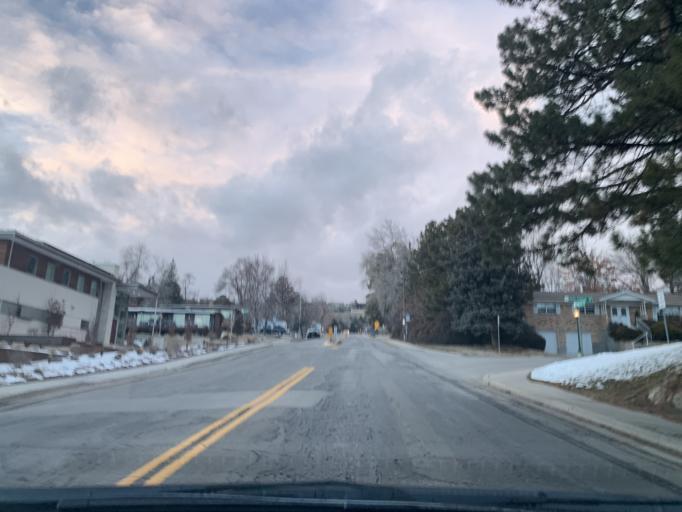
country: US
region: Utah
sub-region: Salt Lake County
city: Salt Lake City
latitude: 40.7745
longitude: -111.8522
